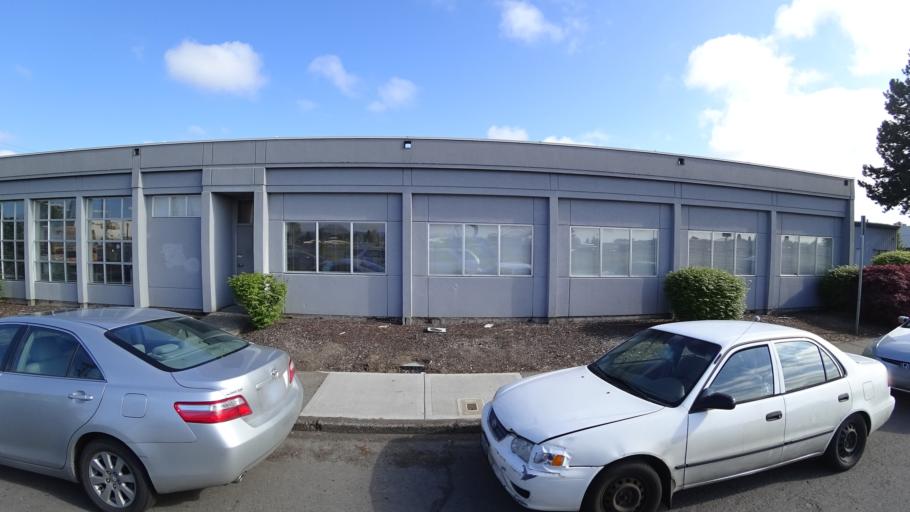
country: US
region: Oregon
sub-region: Washington County
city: Hillsboro
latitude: 45.5177
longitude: -123.0006
